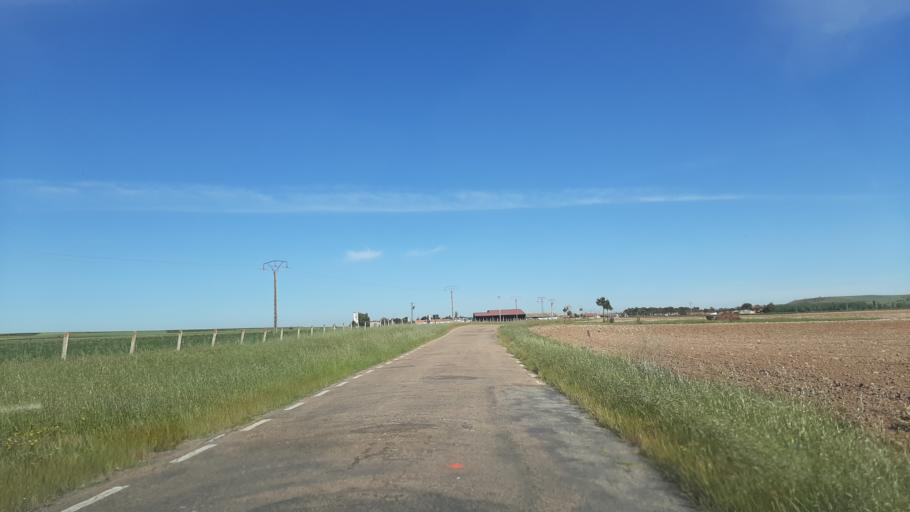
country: ES
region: Castille and Leon
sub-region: Provincia de Salamanca
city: Gajates
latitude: 40.8029
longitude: -5.3786
